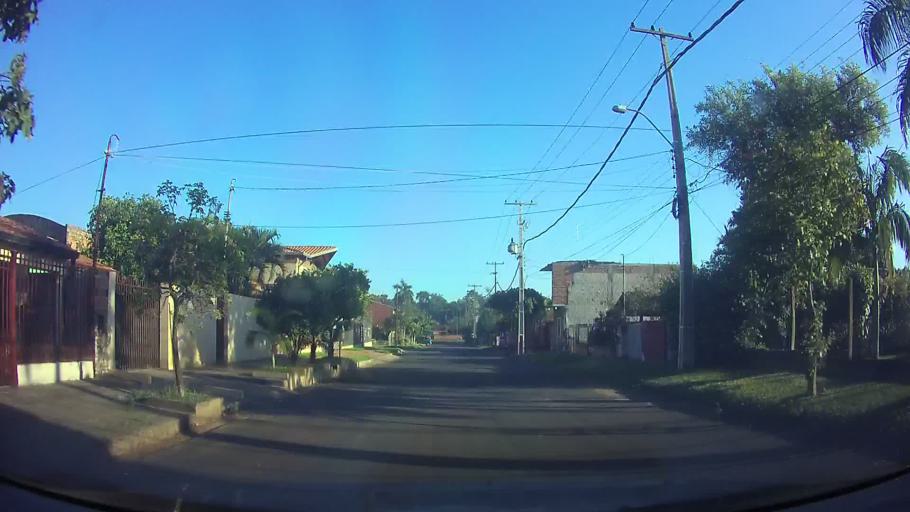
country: PY
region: Central
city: San Lorenzo
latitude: -25.2643
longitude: -57.5005
